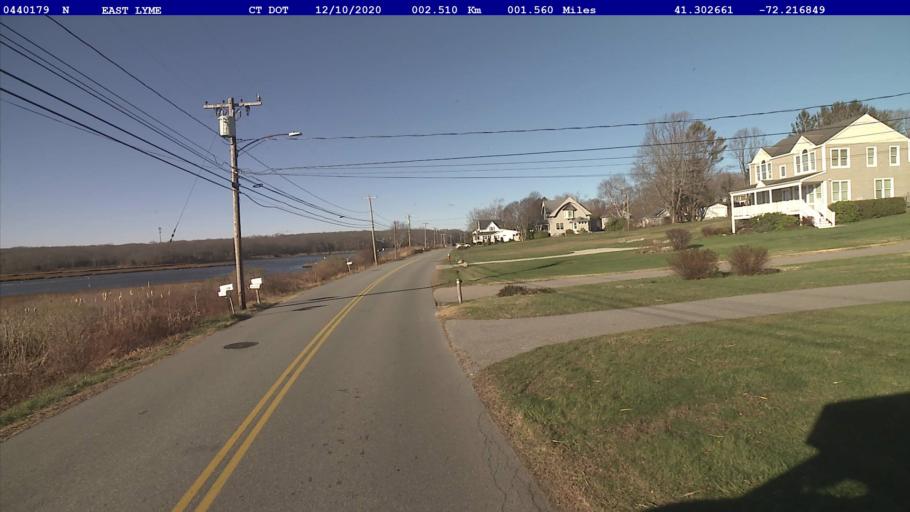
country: US
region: Connecticut
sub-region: New London County
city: Niantic
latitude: 41.3027
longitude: -72.2168
